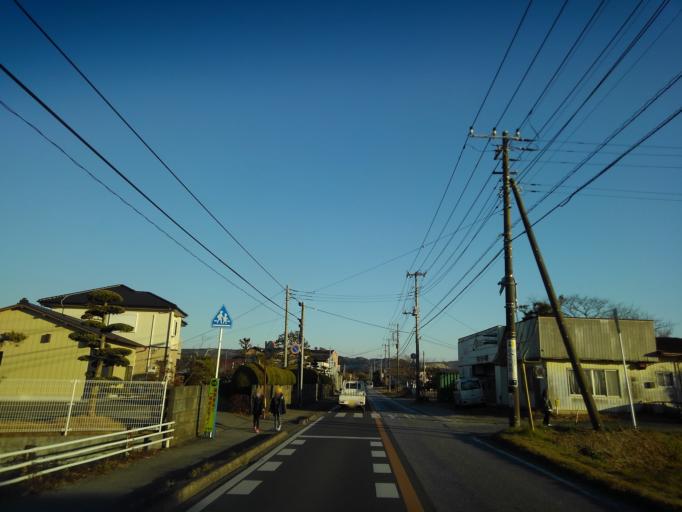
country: JP
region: Chiba
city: Kimitsu
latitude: 35.3036
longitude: 139.9698
